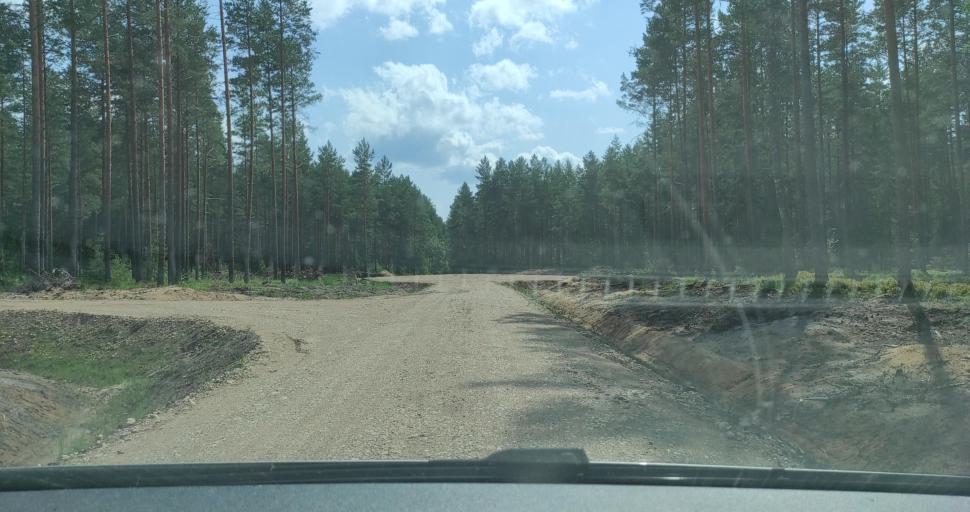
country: LV
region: Kuldigas Rajons
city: Kuldiga
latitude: 57.0535
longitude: 22.1907
